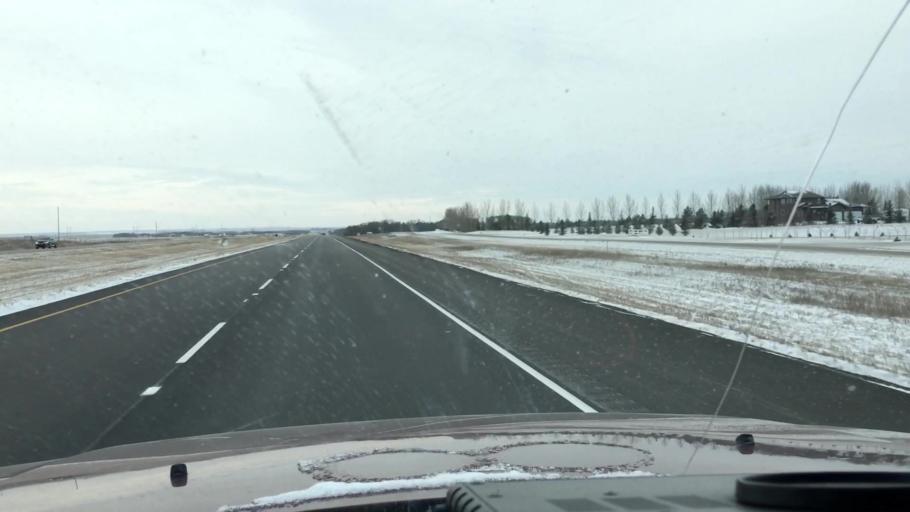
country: CA
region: Saskatchewan
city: Saskatoon
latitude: 51.9081
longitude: -106.5252
